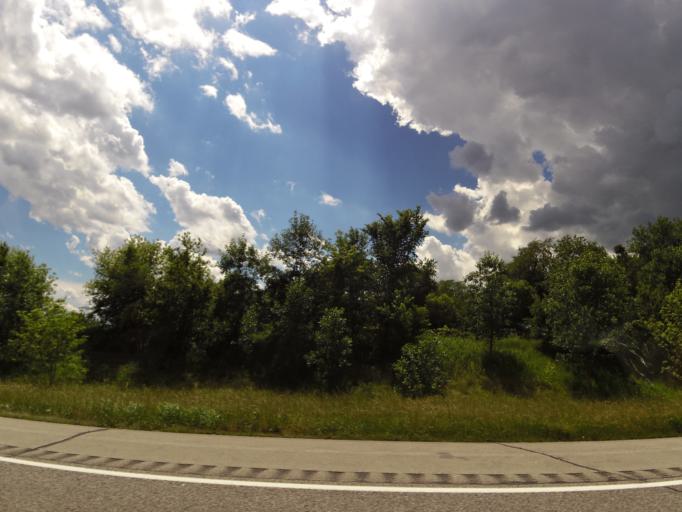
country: US
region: Iowa
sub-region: Linn County
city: Robins
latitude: 42.1164
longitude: -91.7119
